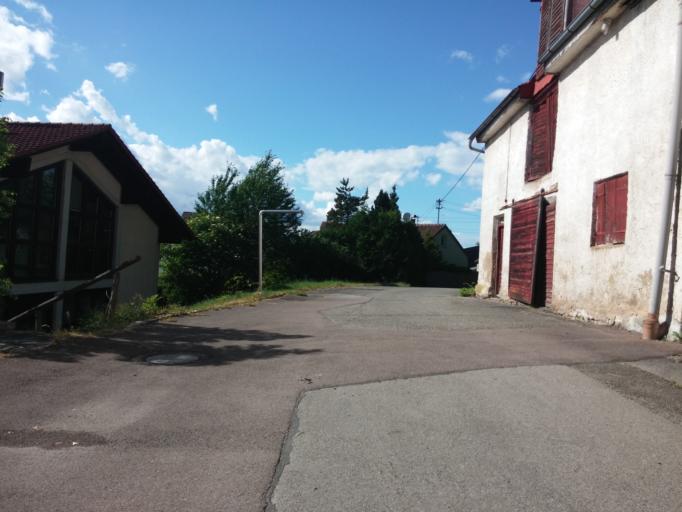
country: DE
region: Bavaria
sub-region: Swabia
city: Illertissen
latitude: 48.2223
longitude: 10.1096
